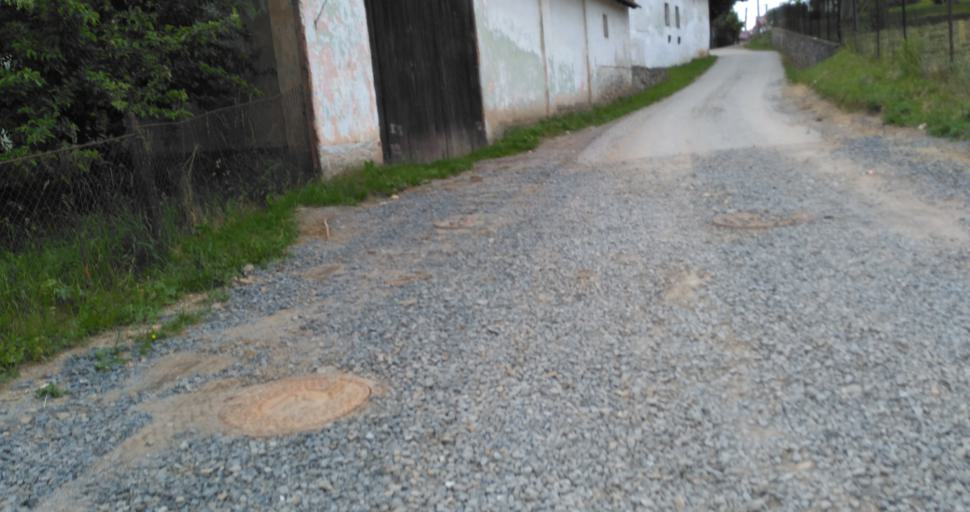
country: CZ
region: South Moravian
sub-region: Okres Blansko
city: Jedovnice
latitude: 49.3361
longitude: 16.7264
